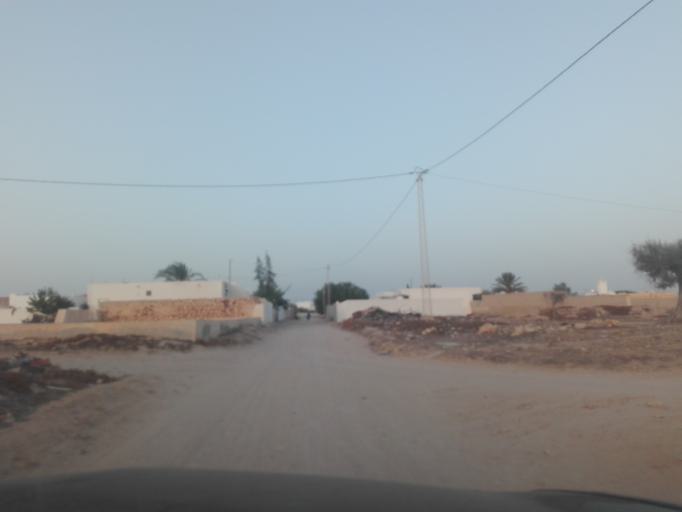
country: TN
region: Madanin
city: Houmt Souk
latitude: 33.7333
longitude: 10.7561
